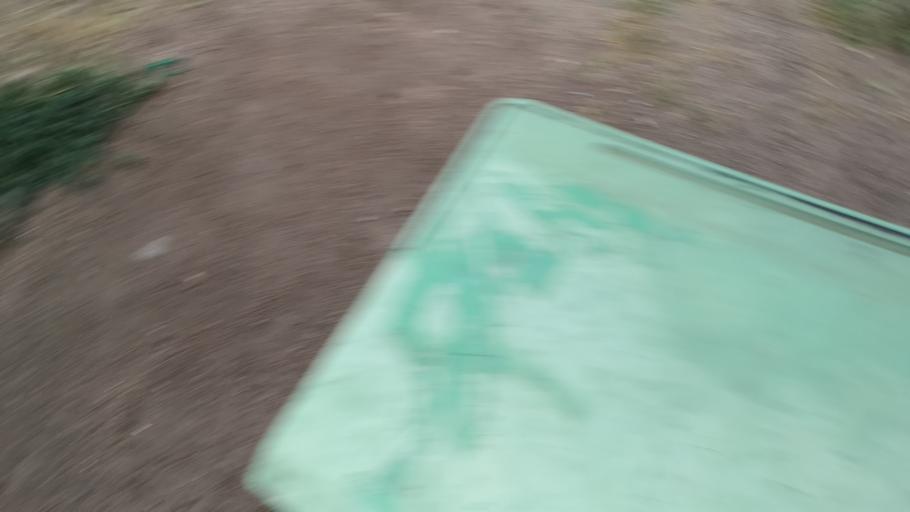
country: YE
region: Sa'dah
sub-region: Monabbih
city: Suq al Khamis
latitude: 17.3807
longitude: 43.1292
